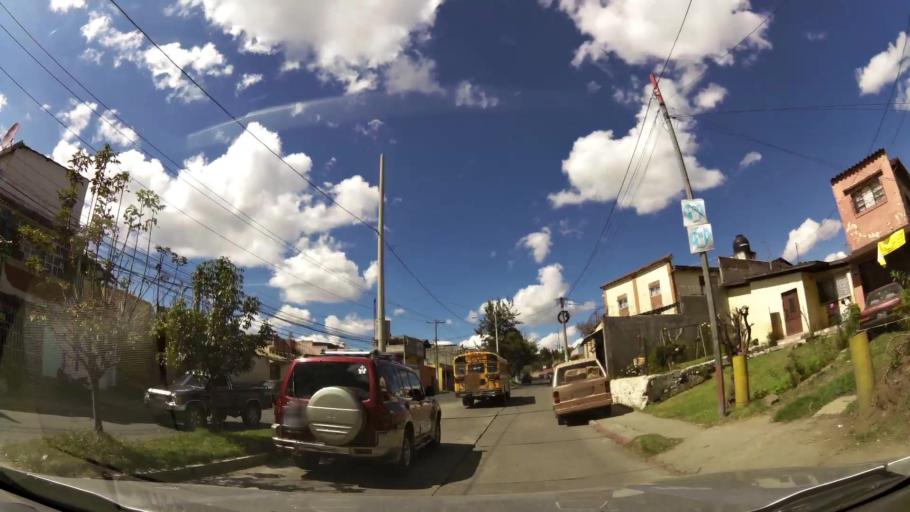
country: GT
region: Quetzaltenango
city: Quetzaltenango
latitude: 14.8428
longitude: -91.5291
